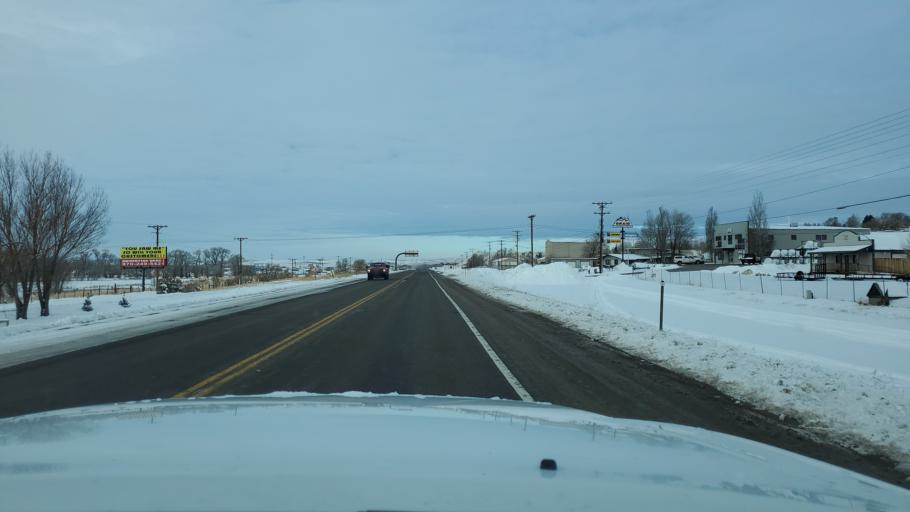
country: US
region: Colorado
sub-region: Moffat County
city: Craig
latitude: 40.5108
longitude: -107.5139
